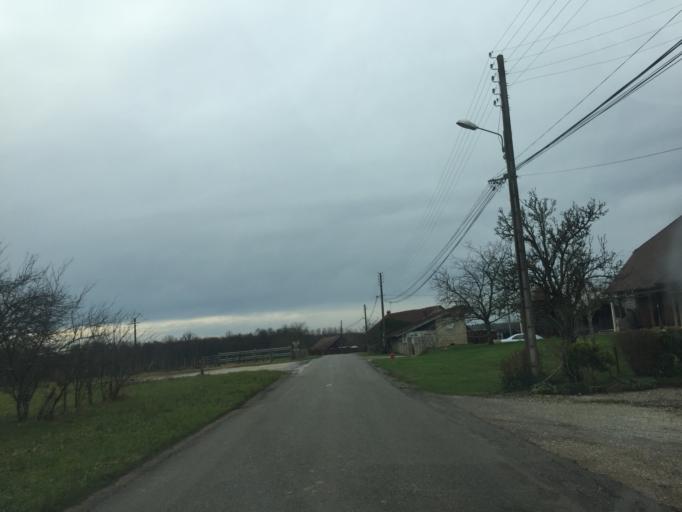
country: FR
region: Franche-Comte
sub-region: Departement du Jura
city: Mont-sous-Vaudrey
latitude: 46.8747
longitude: 5.5355
